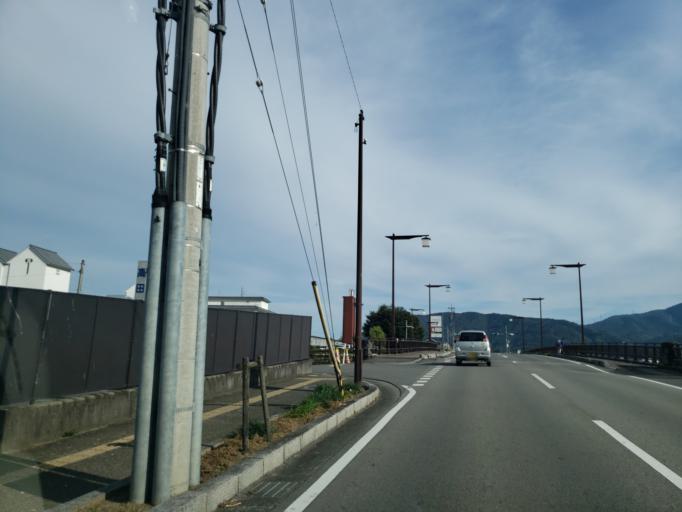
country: JP
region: Tokushima
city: Wakimachi
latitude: 34.0663
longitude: 134.1479
